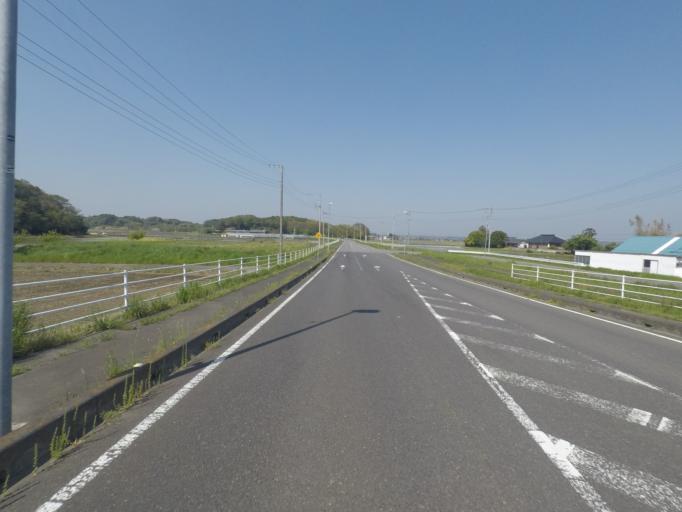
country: JP
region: Ibaraki
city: Inashiki
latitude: 36.0789
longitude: 140.3771
